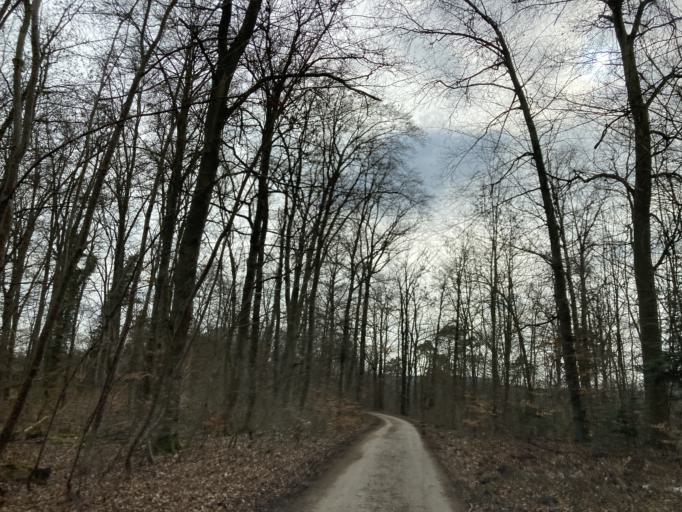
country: DE
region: Baden-Wuerttemberg
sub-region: Tuebingen Region
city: Rottenburg
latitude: 48.4546
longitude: 8.9065
